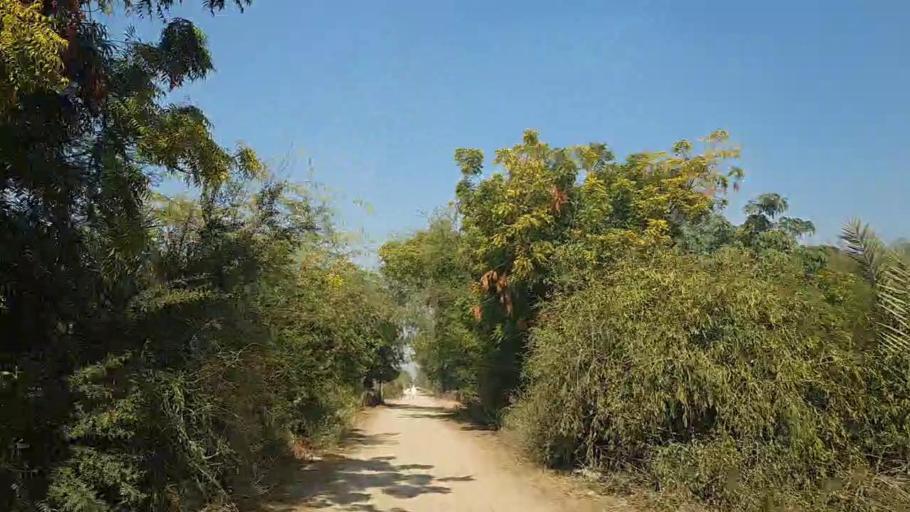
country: PK
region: Sindh
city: Nawabshah
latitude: 26.2404
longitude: 68.3383
